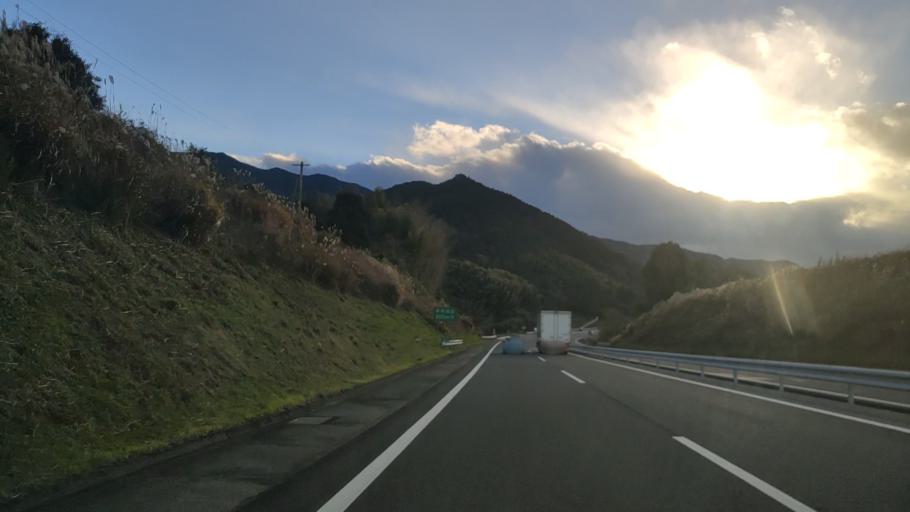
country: JP
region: Ehime
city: Saijo
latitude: 33.8679
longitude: 133.0586
